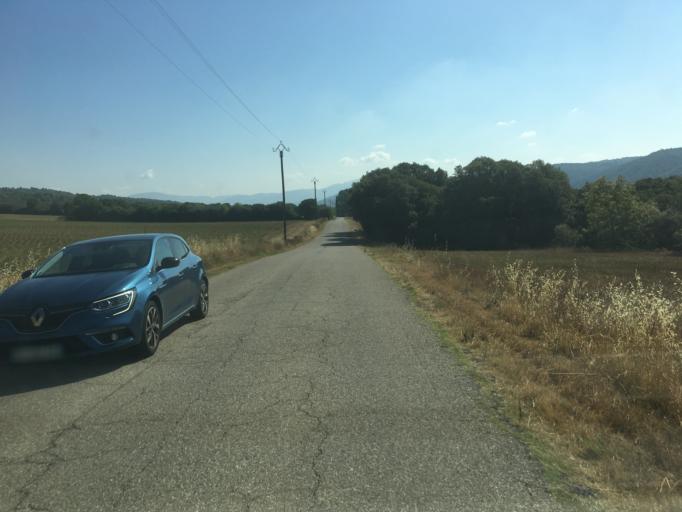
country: FR
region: Provence-Alpes-Cote d'Azur
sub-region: Departement des Alpes-de-Haute-Provence
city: Valensole
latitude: 43.8922
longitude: 5.9715
